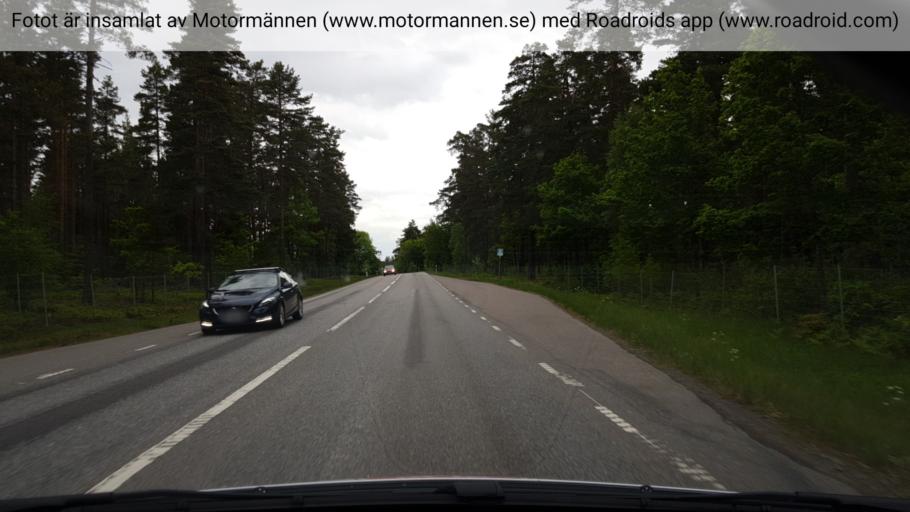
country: SE
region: OErebro
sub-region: Hallsbergs Kommun
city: Palsboda
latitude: 58.9089
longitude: 15.4351
